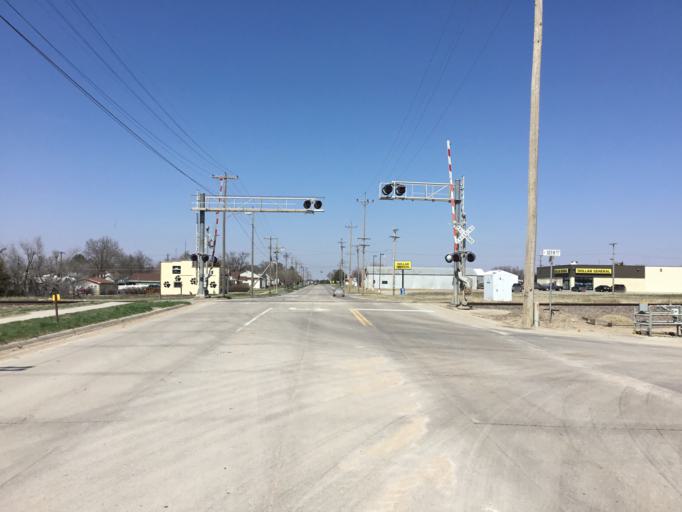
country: US
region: Kansas
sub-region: Russell County
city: Russell
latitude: 38.8949
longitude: -98.8561
